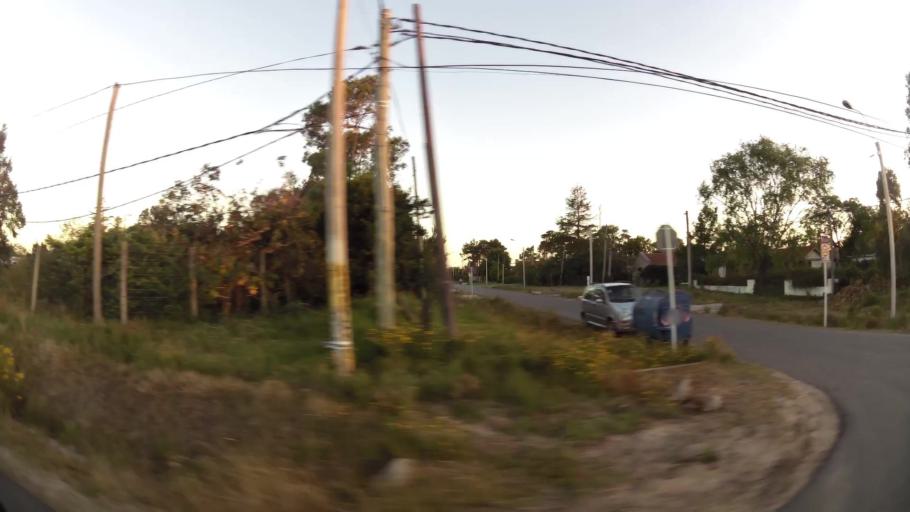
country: UY
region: Canelones
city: Barra de Carrasco
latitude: -34.8364
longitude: -55.9648
